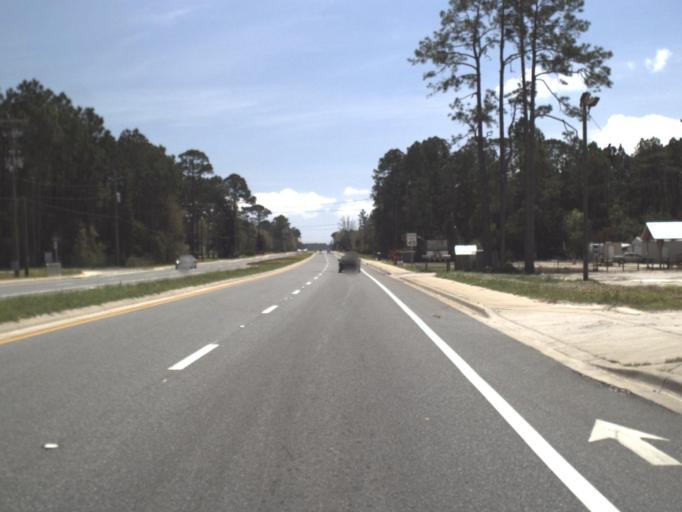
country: US
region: Florida
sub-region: Bay County
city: Laguna Beach
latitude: 30.3327
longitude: -85.8583
